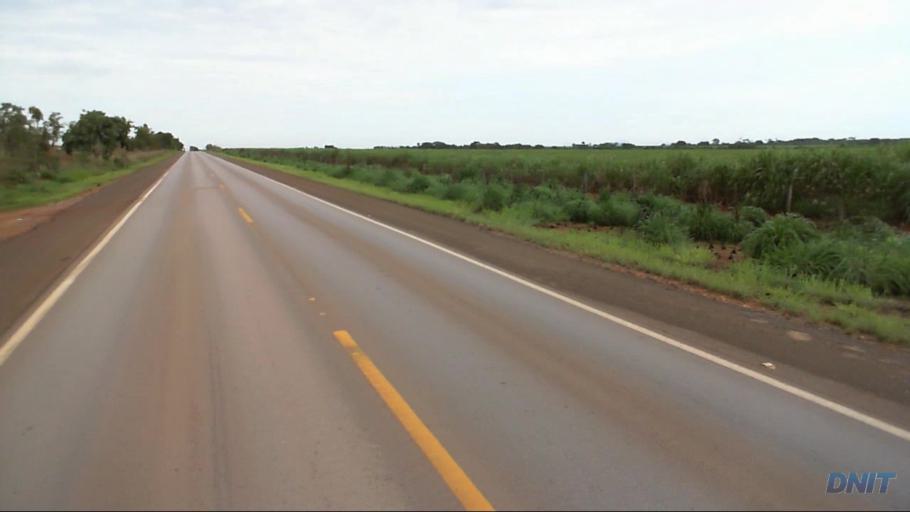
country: BR
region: Goias
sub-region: Uruacu
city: Uruacu
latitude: -14.7195
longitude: -49.1014
